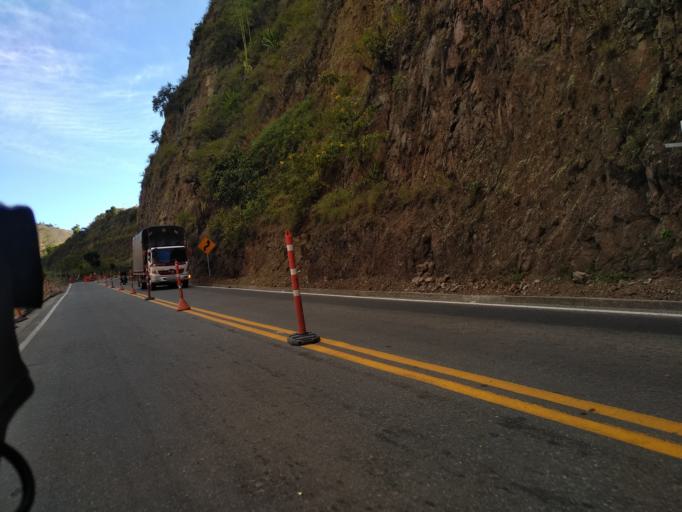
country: CO
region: Narino
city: Imues
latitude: 1.0559
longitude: -77.4495
